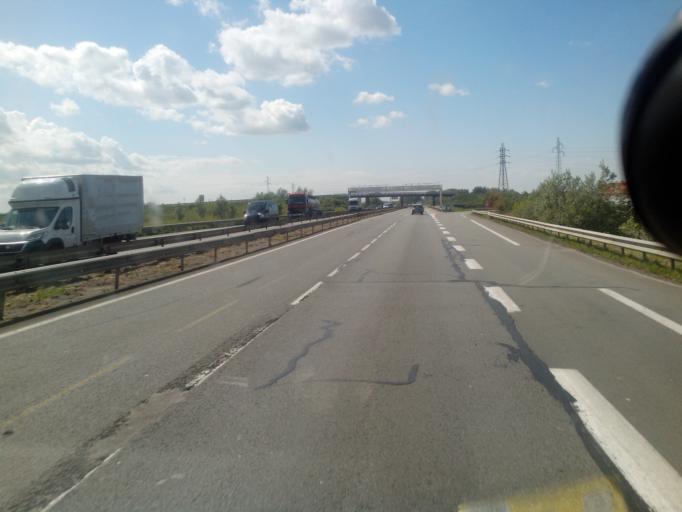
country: FR
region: Nord-Pas-de-Calais
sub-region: Departement du Nord
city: Cappelle-la-Grande
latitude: 50.9886
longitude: 2.3588
